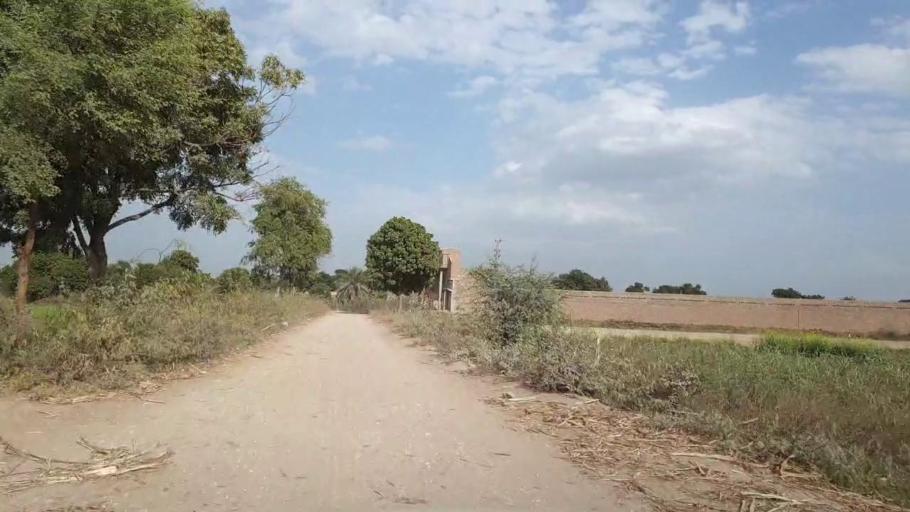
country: PK
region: Sindh
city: Matiari
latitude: 25.5570
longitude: 68.5737
